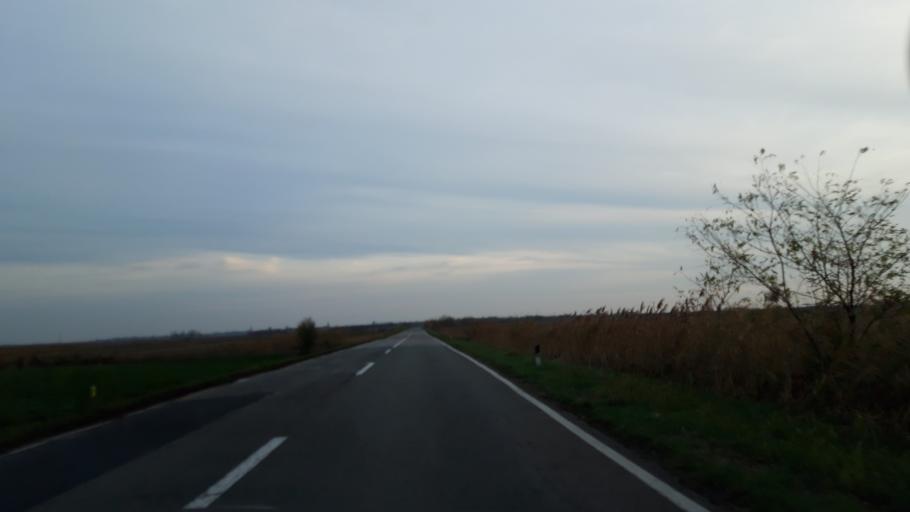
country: RS
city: Ostojicevo
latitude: 45.9127
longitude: 20.1514
